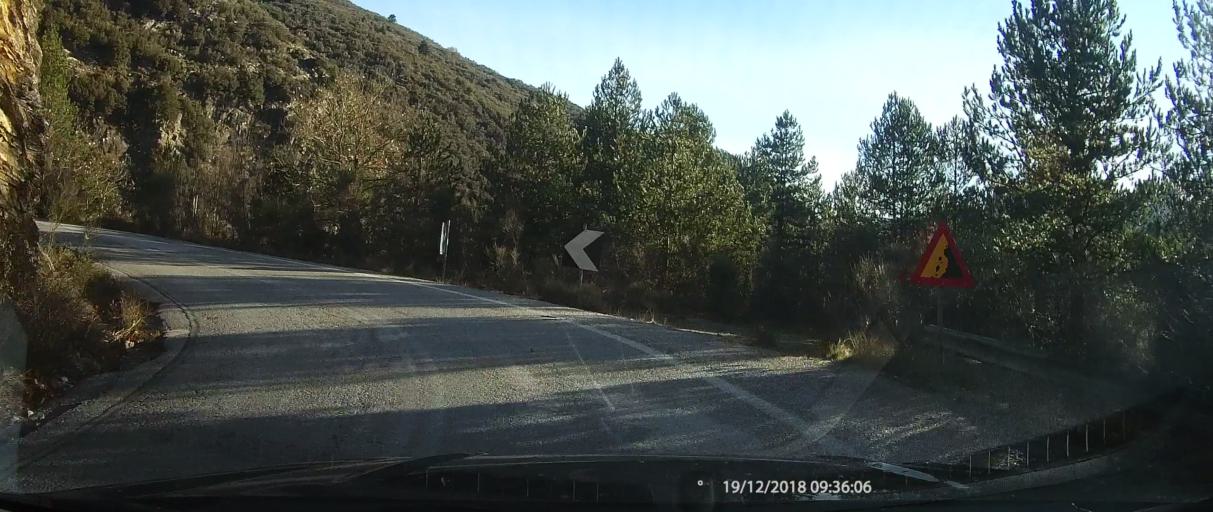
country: GR
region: Peloponnese
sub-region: Nomos Lakonias
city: Magoula
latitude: 37.0801
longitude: 22.2840
